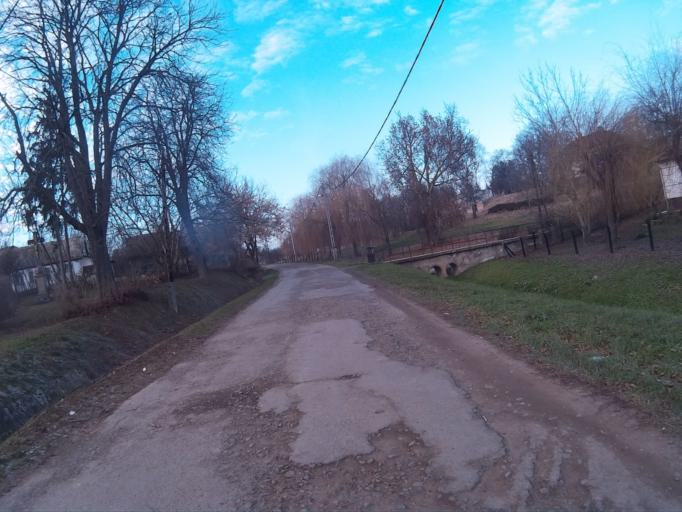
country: HU
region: Nograd
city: Bercel
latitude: 47.9776
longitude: 19.4246
